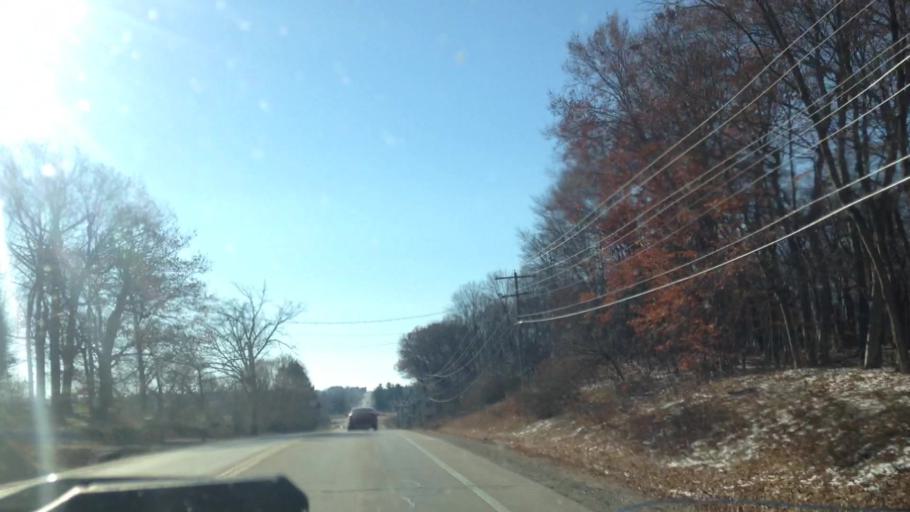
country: US
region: Wisconsin
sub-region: Washington County
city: West Bend
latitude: 43.4027
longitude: -88.1612
